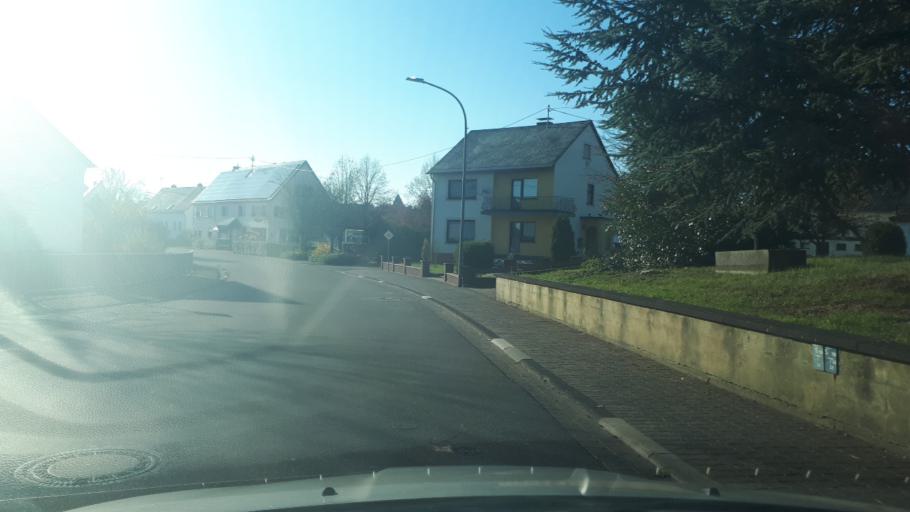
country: DE
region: Rheinland-Pfalz
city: Weiler
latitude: 50.1527
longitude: 7.0848
